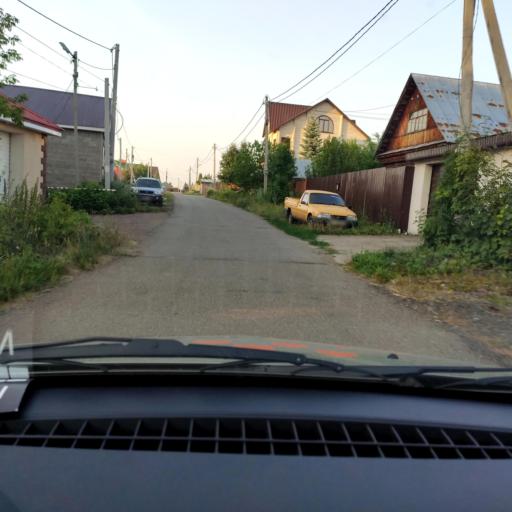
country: RU
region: Bashkortostan
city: Avdon
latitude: 54.5864
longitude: 55.6745
